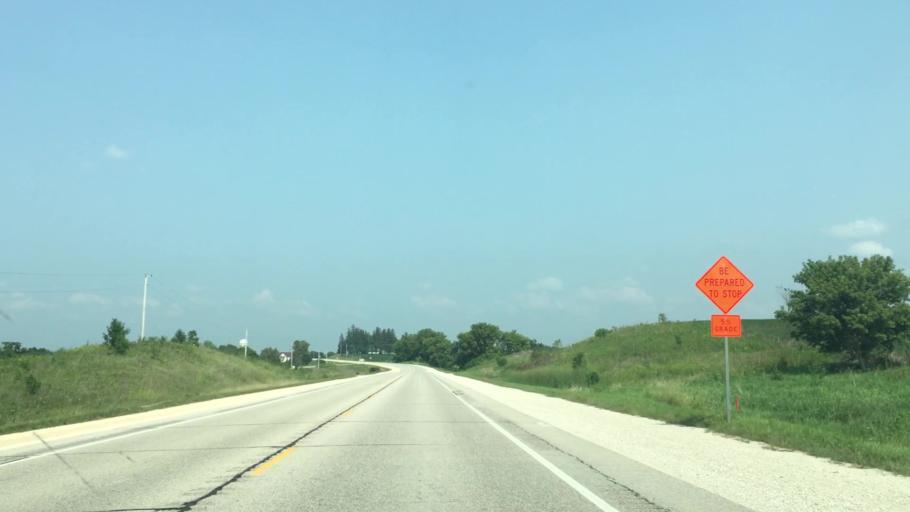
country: US
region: Iowa
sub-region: Winneshiek County
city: Decorah
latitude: 43.2760
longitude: -91.8184
